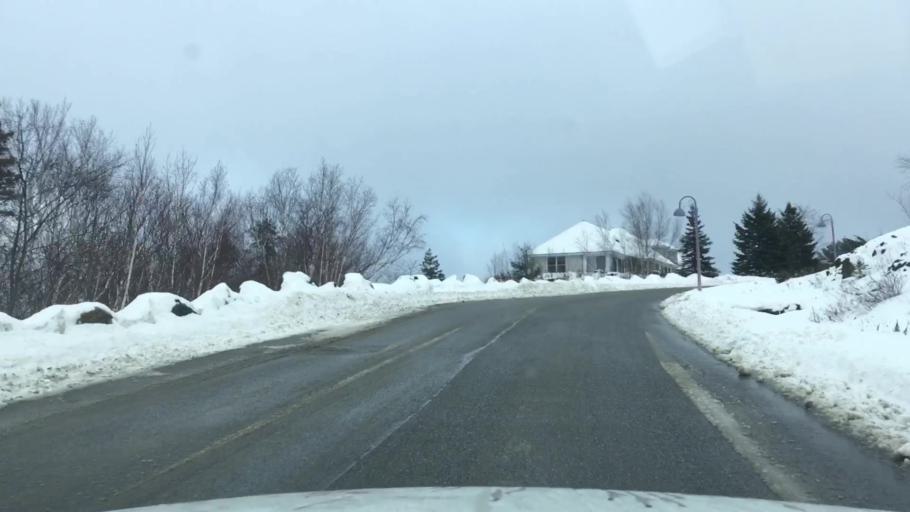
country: US
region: Maine
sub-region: Hancock County
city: Bar Harbor
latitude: 44.4146
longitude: -68.2596
